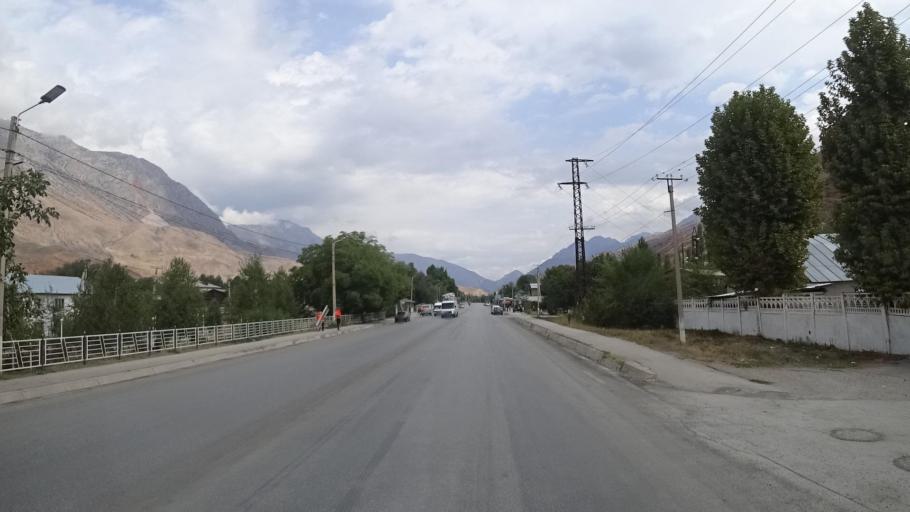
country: KG
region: Jalal-Abad
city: Toktogul
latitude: 41.6319
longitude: 72.6899
